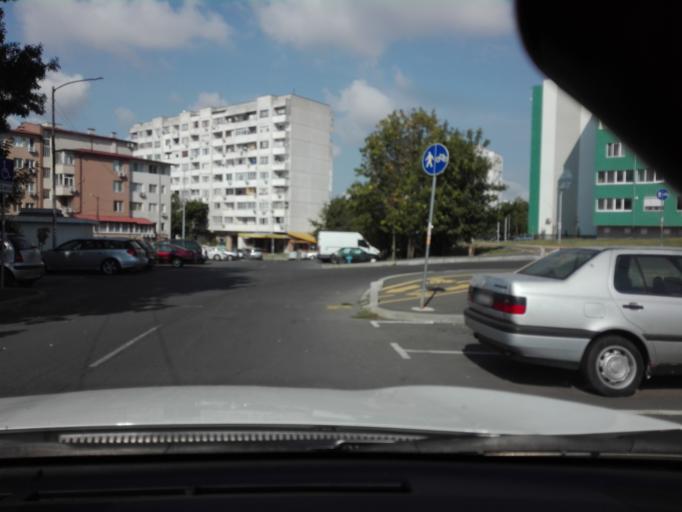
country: BG
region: Burgas
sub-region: Obshtina Burgas
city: Burgas
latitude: 42.4556
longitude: 27.4205
